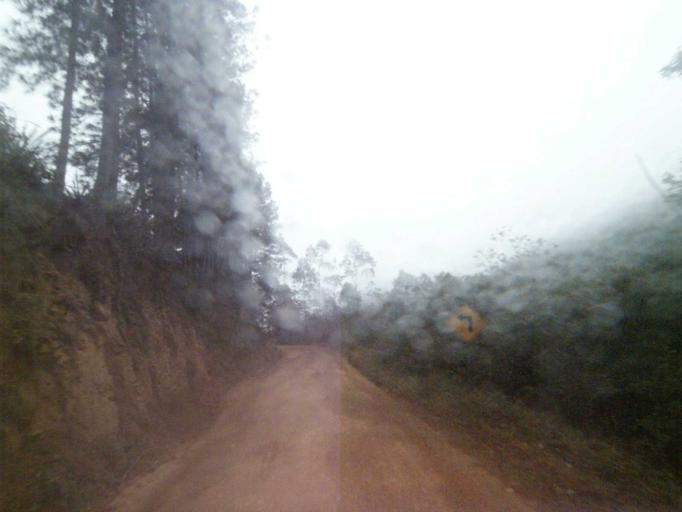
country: BR
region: Santa Catarina
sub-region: Anitapolis
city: Anitapolis
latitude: -27.8839
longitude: -49.1327
